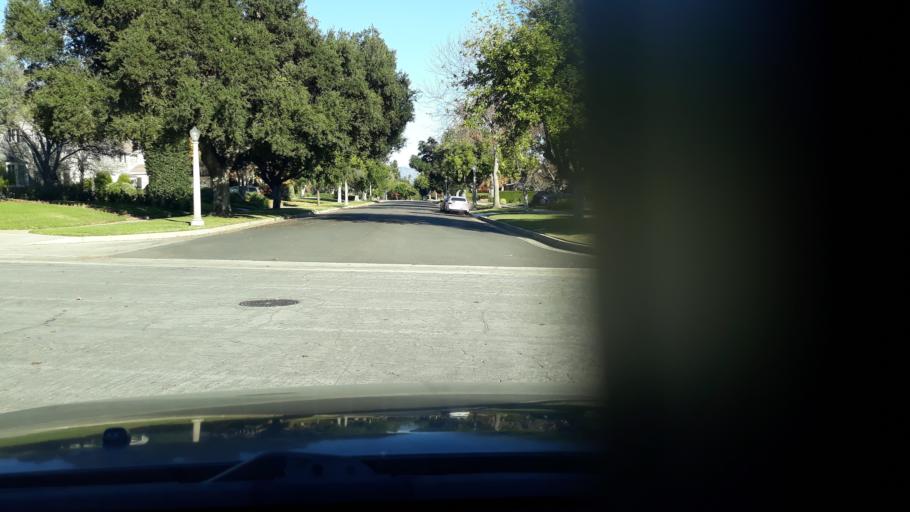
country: US
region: California
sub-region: Los Angeles County
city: San Marino
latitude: 34.1187
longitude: -118.1035
